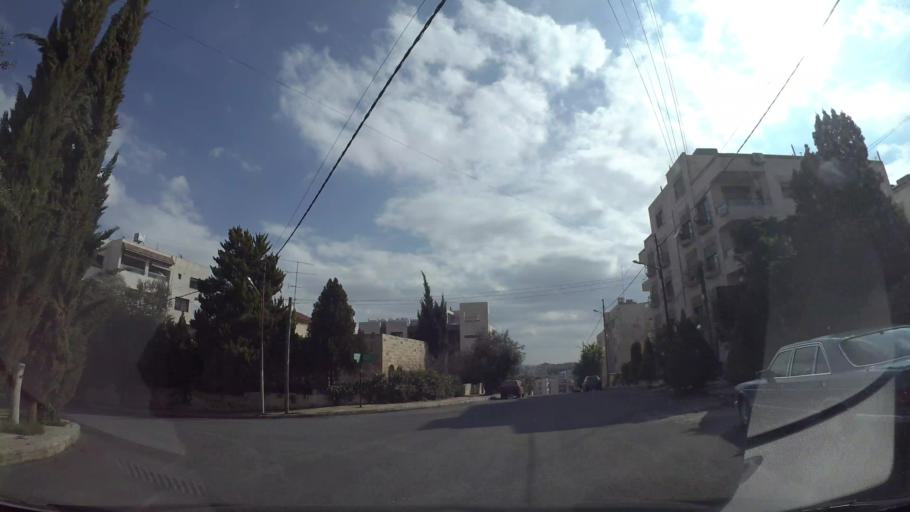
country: JO
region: Amman
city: Amman
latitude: 31.9704
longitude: 35.8893
